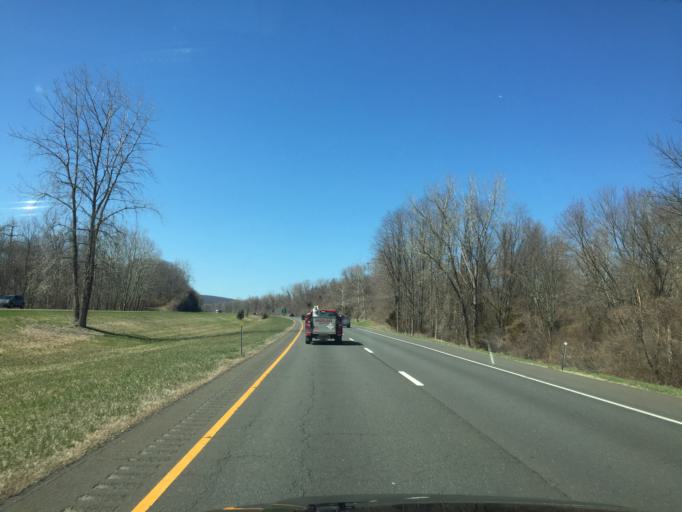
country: US
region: Connecticut
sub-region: Fairfield County
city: Danbury
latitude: 41.4576
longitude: -73.3965
